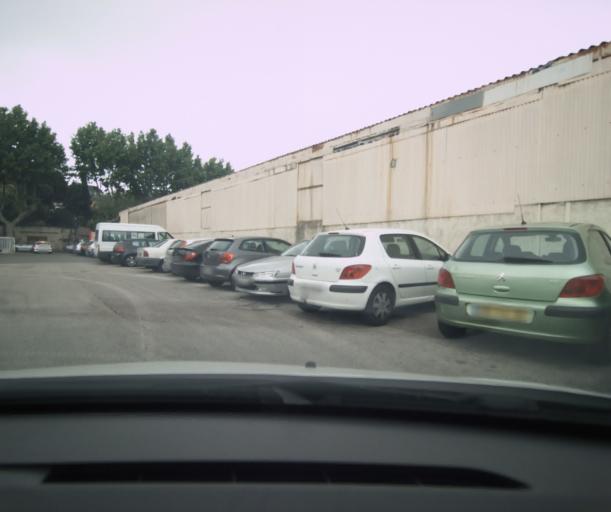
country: FR
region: Provence-Alpes-Cote d'Azur
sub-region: Departement du Var
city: Toulon
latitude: 43.1214
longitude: 5.9549
